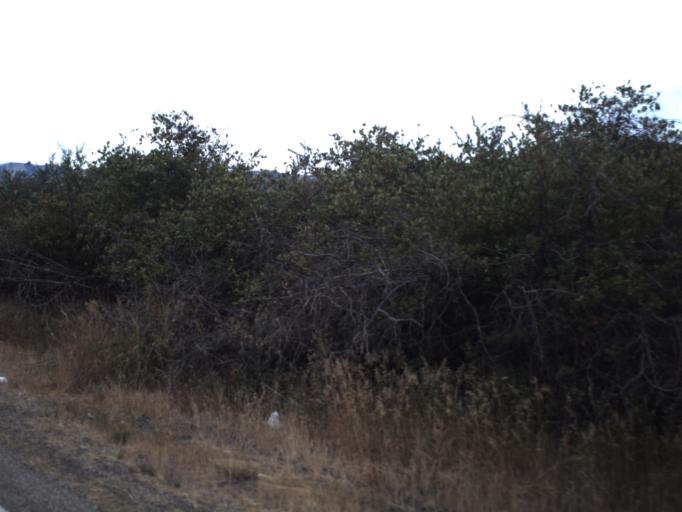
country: US
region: Utah
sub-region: Morgan County
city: Morgan
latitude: 41.0052
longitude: -111.6758
